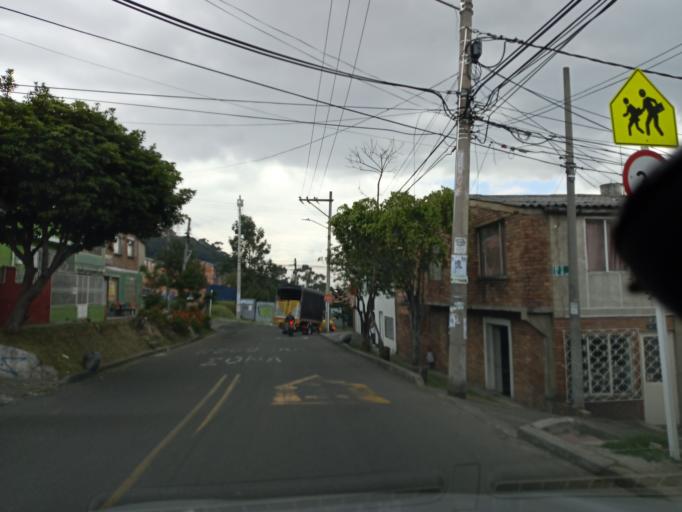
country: CO
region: Bogota D.C.
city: Bogota
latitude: 4.5680
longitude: -74.1056
